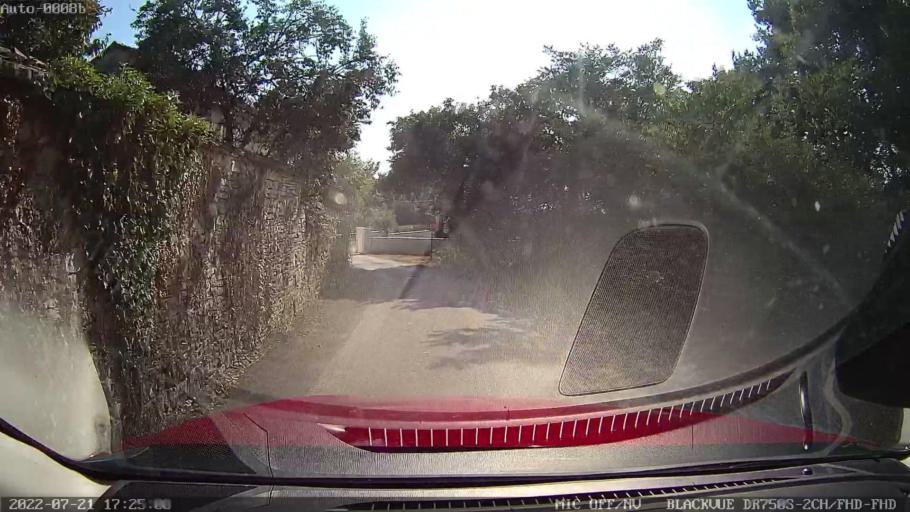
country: HR
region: Istarska
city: Karojba
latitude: 45.1846
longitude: 13.8200
